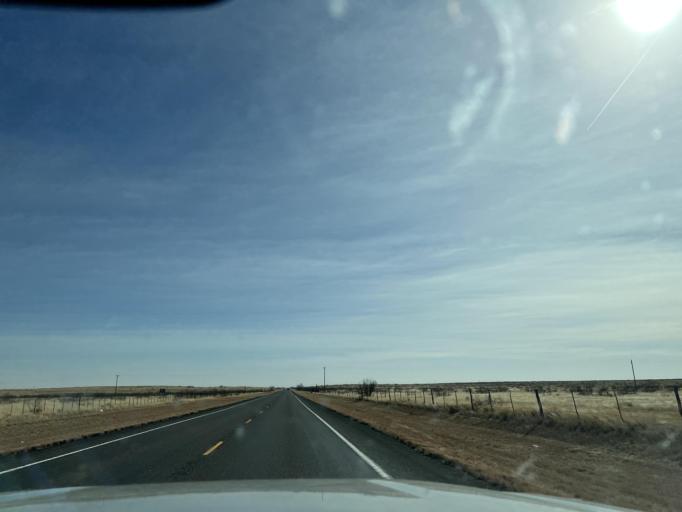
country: US
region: Texas
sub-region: Andrews County
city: Andrews
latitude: 32.4824
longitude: -102.4777
